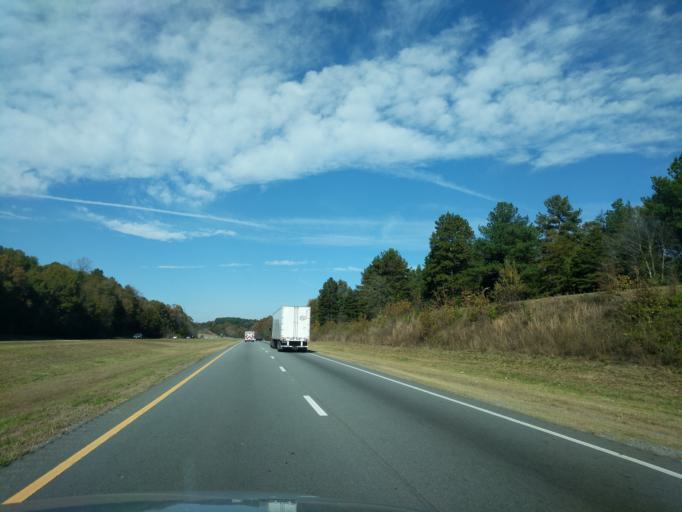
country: US
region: North Carolina
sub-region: Gaston County
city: Dallas
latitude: 35.3357
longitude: -81.1917
